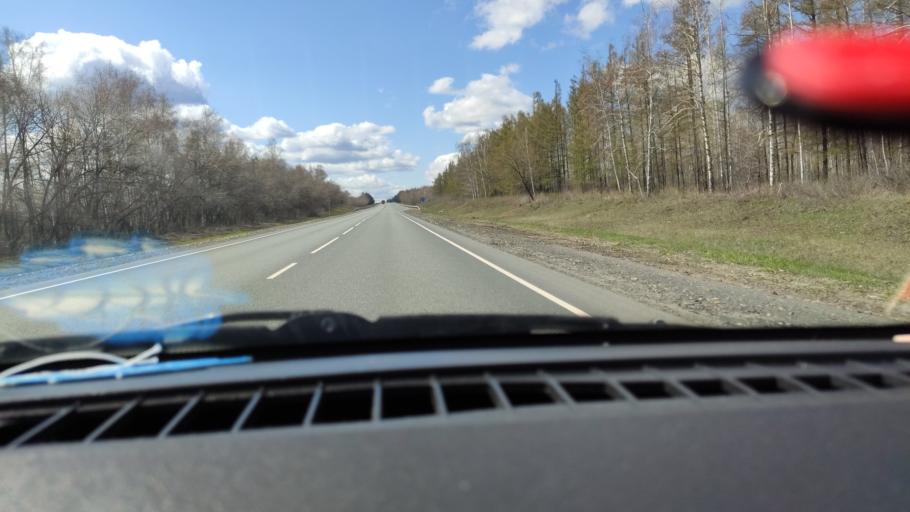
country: RU
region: Saratov
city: Khvalynsk
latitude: 52.5649
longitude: 48.0940
